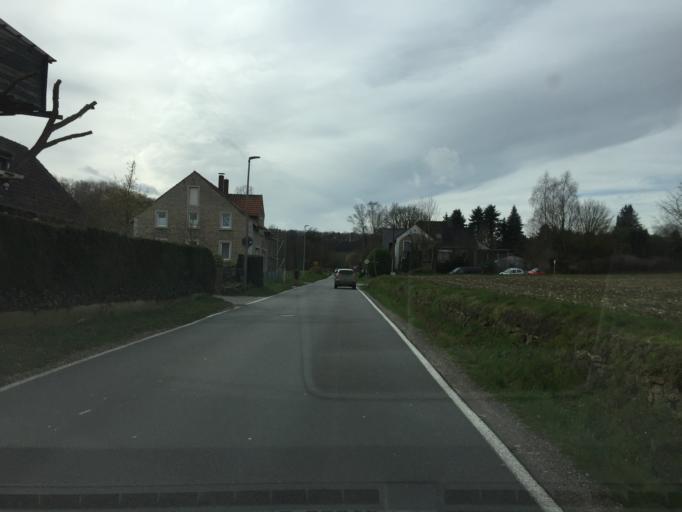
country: DE
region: North Rhine-Westphalia
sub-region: Regierungsbezirk Detmold
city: Detmold
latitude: 51.9397
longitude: 8.8328
